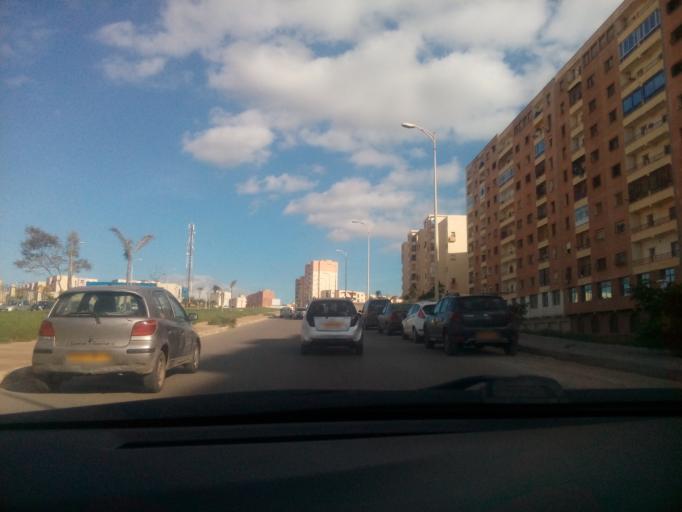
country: DZ
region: Oran
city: Bir el Djir
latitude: 35.7004
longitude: -0.5669
